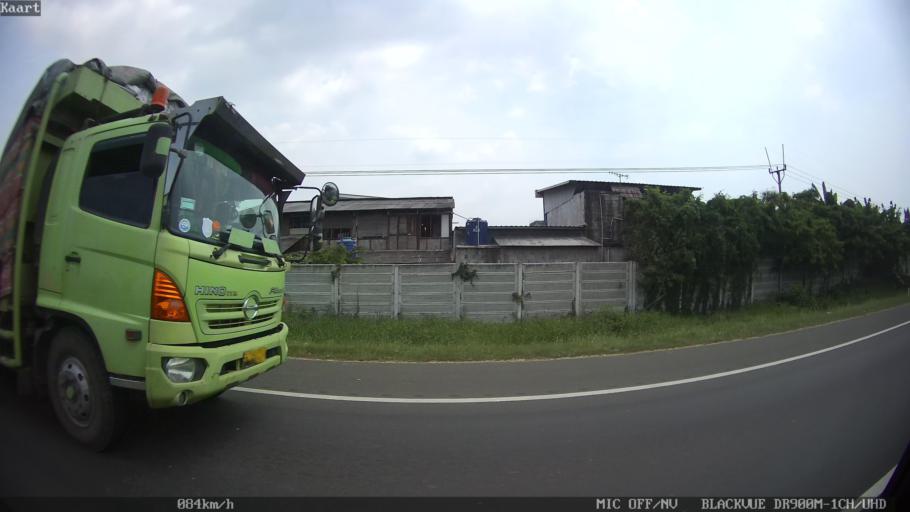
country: ID
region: Banten
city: Bojonegara
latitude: -6.0133
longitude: 106.0805
